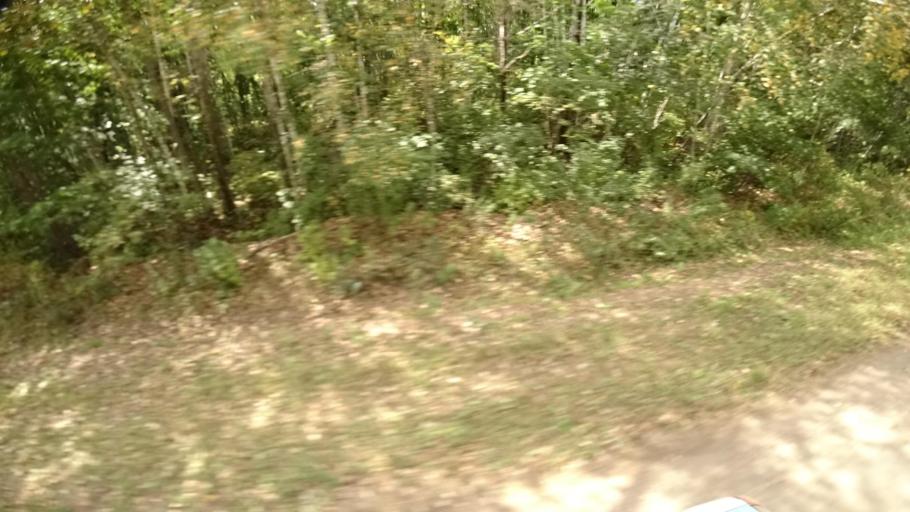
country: RU
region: Primorskiy
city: Yakovlevka
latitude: 44.7032
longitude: 133.6497
